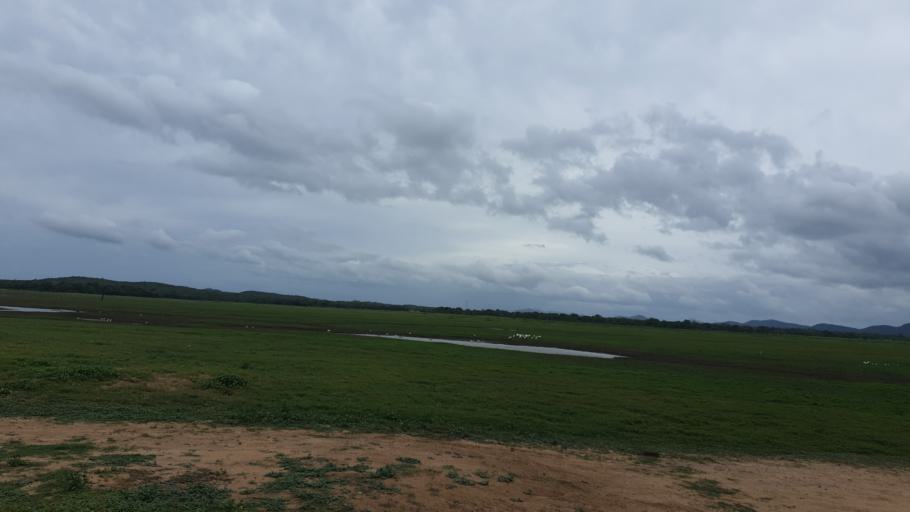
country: LK
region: North Central
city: Polonnaruwa
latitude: 8.1289
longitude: 80.9081
